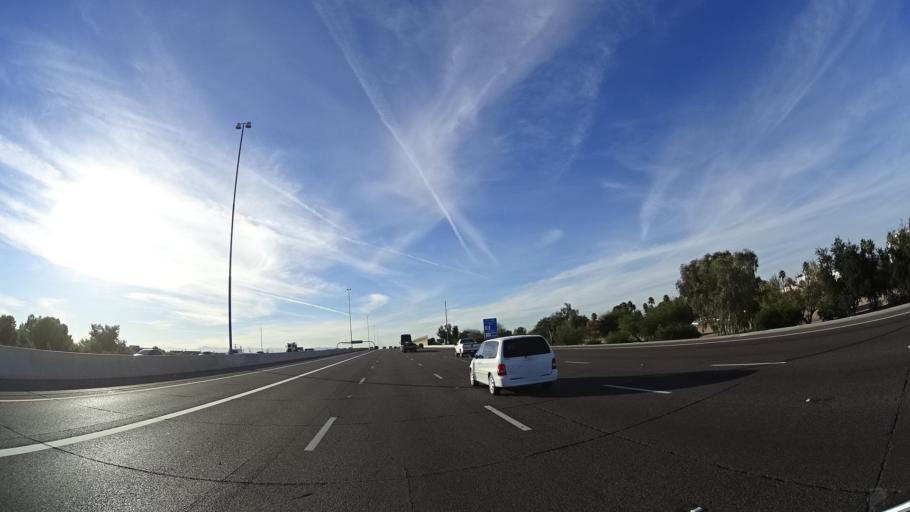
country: US
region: Arizona
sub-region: Maricopa County
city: Gilbert
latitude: 33.3864
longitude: -111.6987
